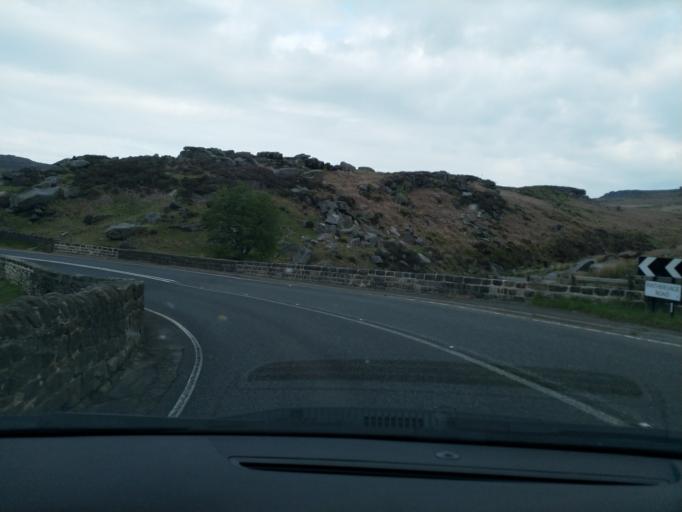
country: GB
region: England
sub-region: Derbyshire
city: Hathersage
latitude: 53.3226
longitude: -1.6087
